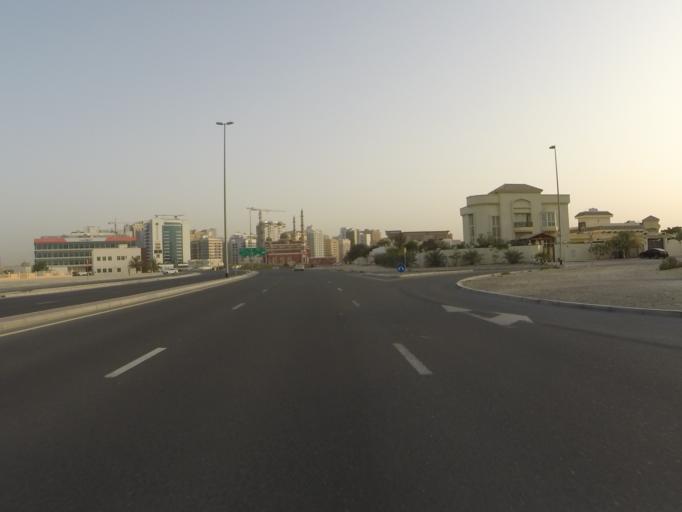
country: AE
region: Dubai
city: Dubai
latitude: 25.1045
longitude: 55.2059
